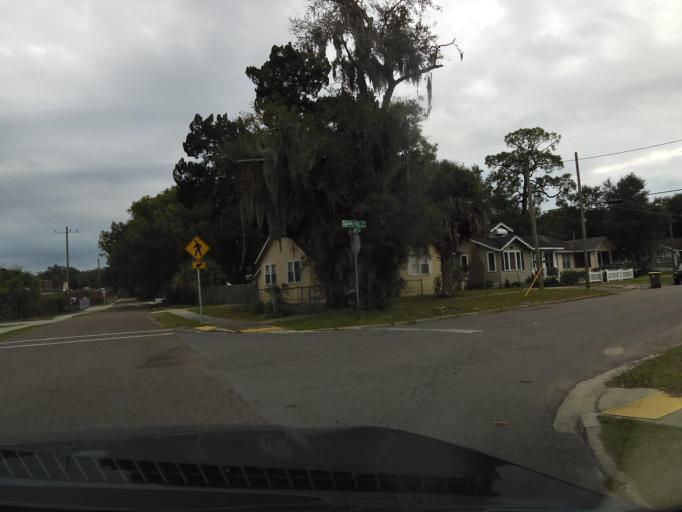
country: US
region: Florida
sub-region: Duval County
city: Jacksonville
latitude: 30.3692
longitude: -81.6591
